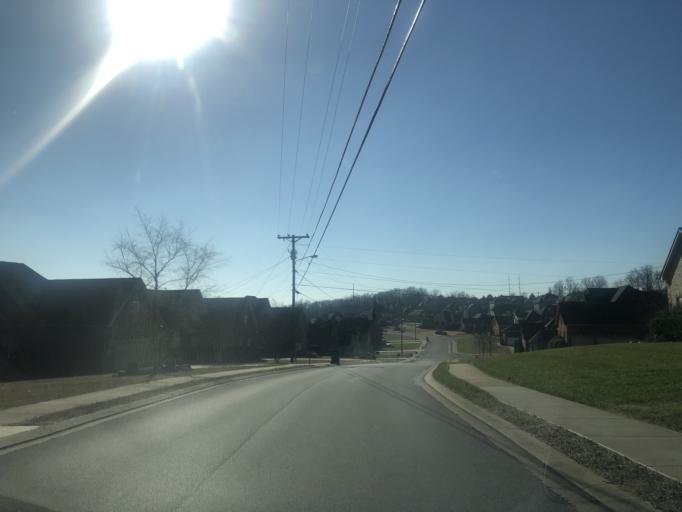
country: US
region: Tennessee
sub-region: Rutherford County
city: Smyrna
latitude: 35.9680
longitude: -86.5412
